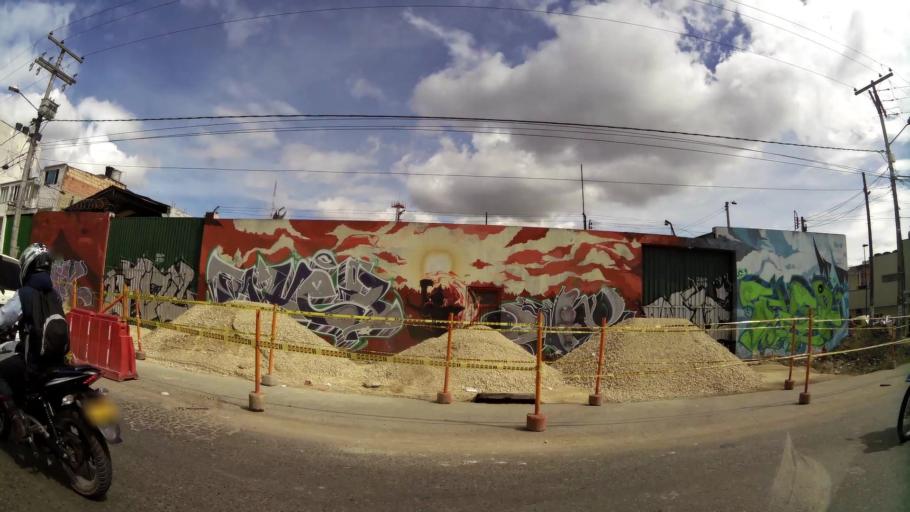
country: CO
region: Bogota D.C.
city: Bogota
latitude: 4.6146
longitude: -74.1347
